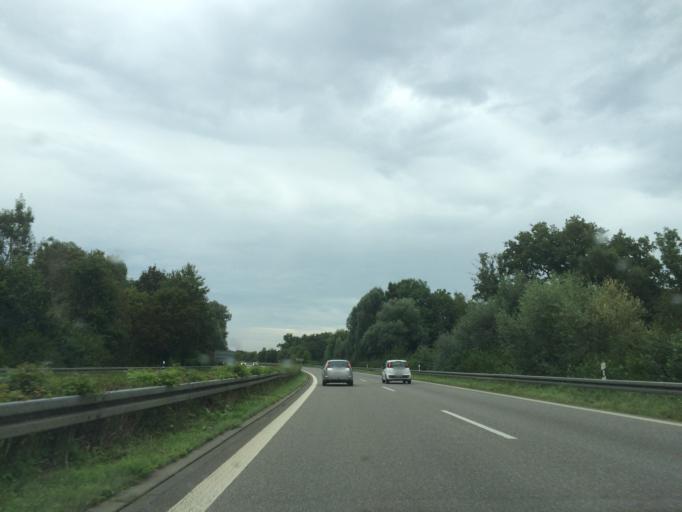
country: DE
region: Baden-Wuerttemberg
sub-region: Tuebingen Region
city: Berg
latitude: 47.8213
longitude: 9.6144
